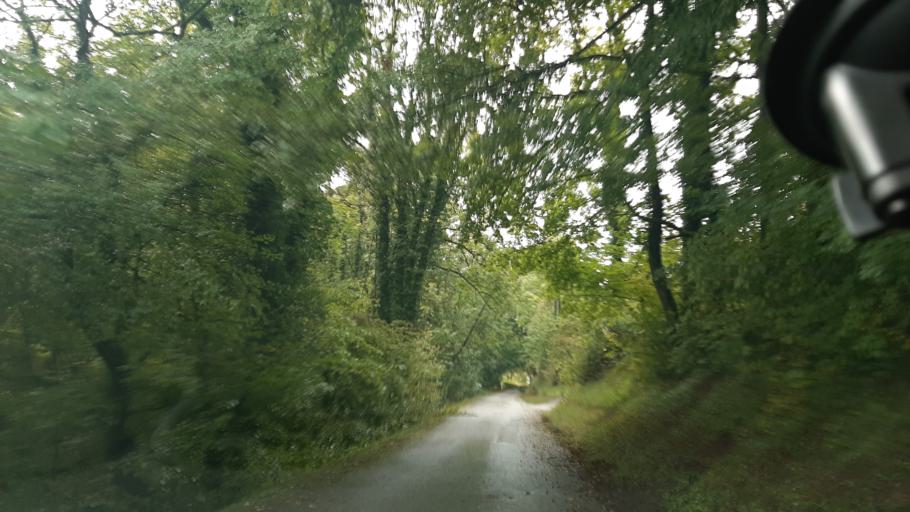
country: FR
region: Rhone-Alpes
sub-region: Departement de la Savoie
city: Gresy-sur-Isere
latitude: 45.6146
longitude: 6.2698
